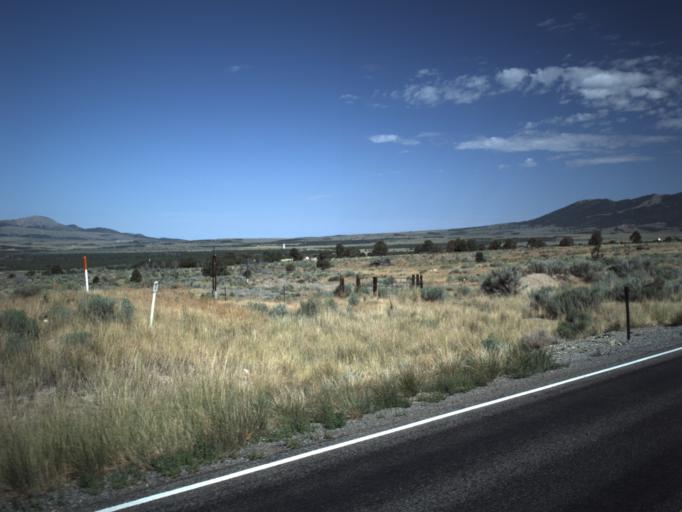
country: US
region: Utah
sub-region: Juab County
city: Mona
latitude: 39.9163
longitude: -112.1432
